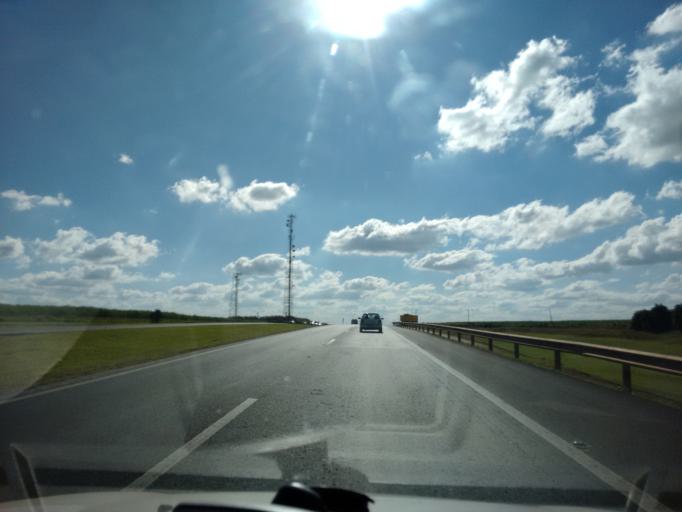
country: BR
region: Sao Paulo
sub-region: Araraquara
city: Araraquara
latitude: -21.8632
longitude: -48.1158
